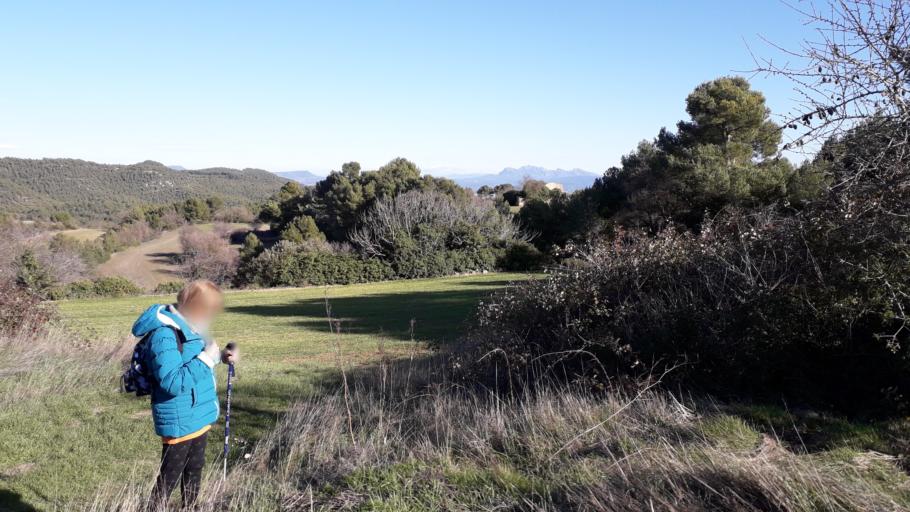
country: ES
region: Catalonia
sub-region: Provincia de Barcelona
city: Bellprat
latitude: 41.5581
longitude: 1.4568
